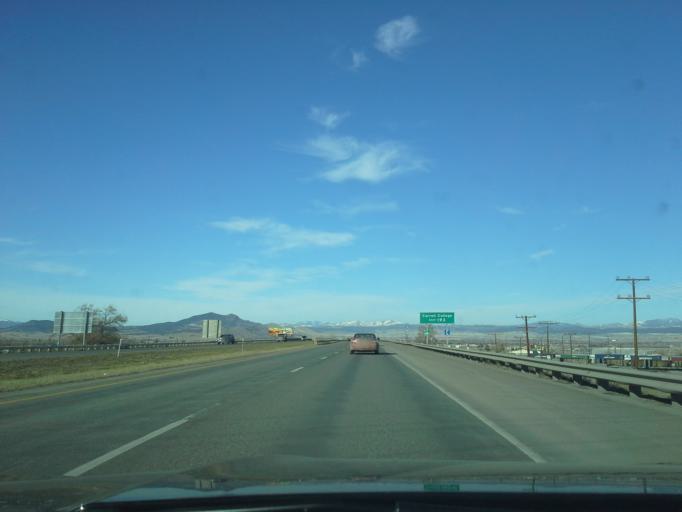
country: US
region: Montana
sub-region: Lewis and Clark County
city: Helena
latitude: 46.5956
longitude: -112.0013
